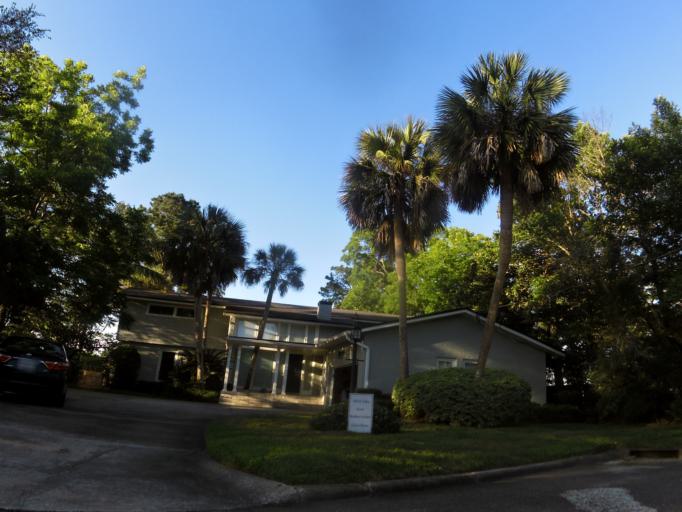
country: US
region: Florida
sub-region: Clay County
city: Orange Park
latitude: 30.2483
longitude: -81.6885
